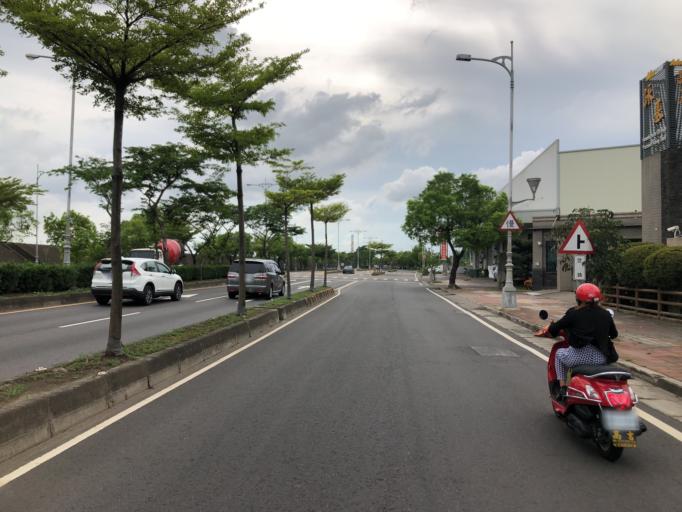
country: TW
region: Taiwan
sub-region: Taichung City
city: Taichung
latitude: 24.0945
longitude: 120.6372
